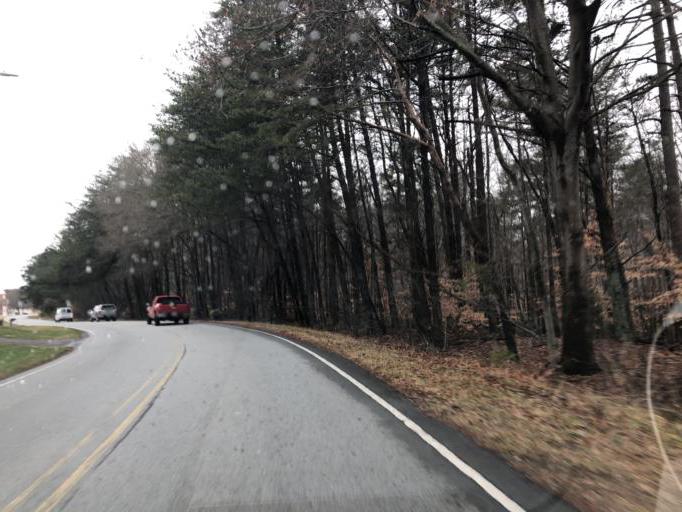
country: US
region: North Carolina
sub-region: Gaston County
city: Ranlo
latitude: 35.2951
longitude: -81.1206
